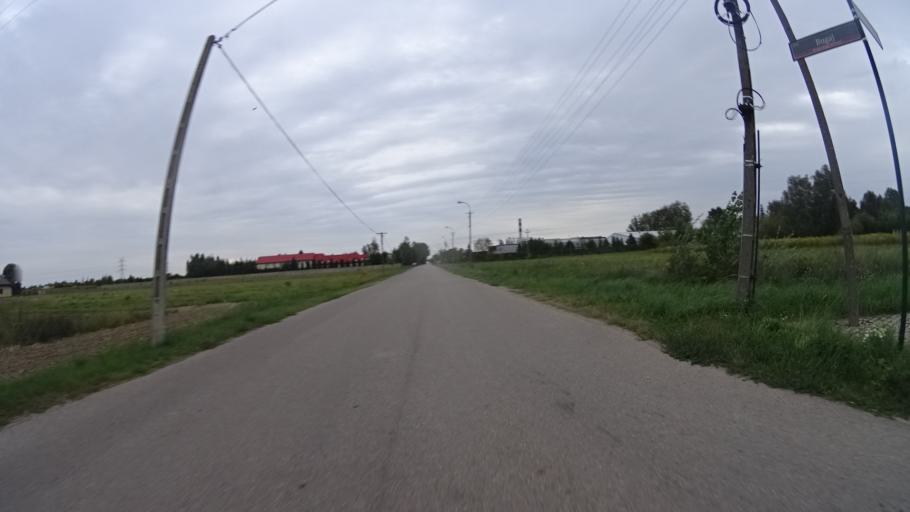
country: PL
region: Masovian Voivodeship
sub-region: Powiat warszawski zachodni
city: Ozarow Mazowiecki
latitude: 52.2461
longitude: 20.7866
